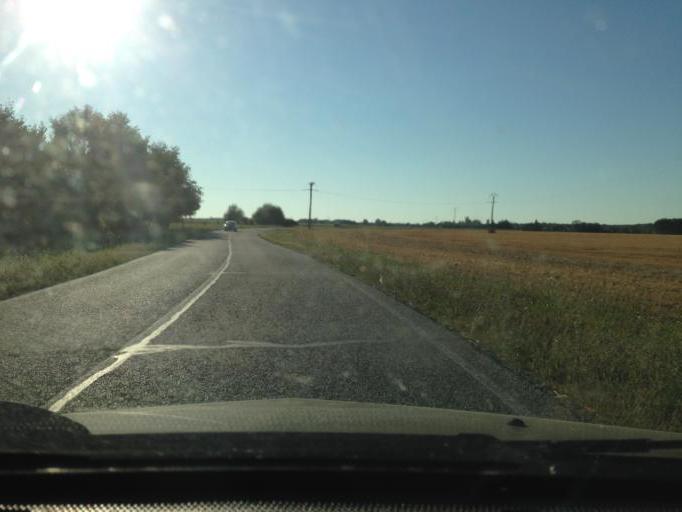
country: FR
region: Ile-de-France
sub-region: Departement des Yvelines
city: Magny-les-Hameaux
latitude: 48.7354
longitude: 2.0709
